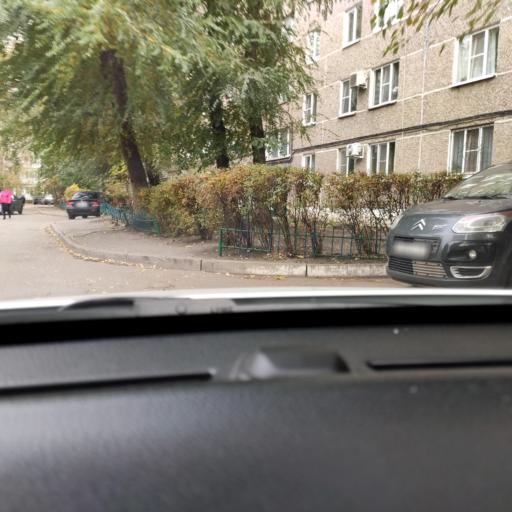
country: RU
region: Voronezj
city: Pridonskoy
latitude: 51.6827
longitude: 39.0882
